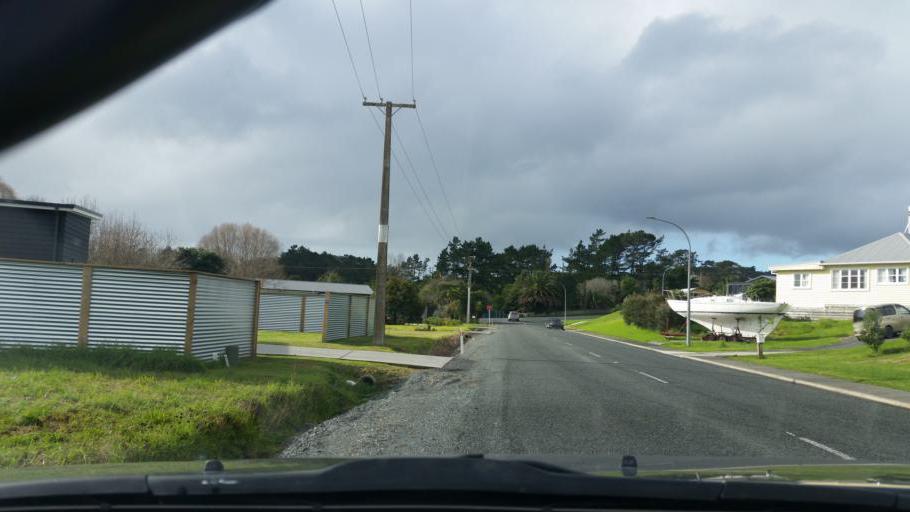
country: NZ
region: Auckland
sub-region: Auckland
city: Wellsford
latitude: -36.0864
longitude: 174.5764
